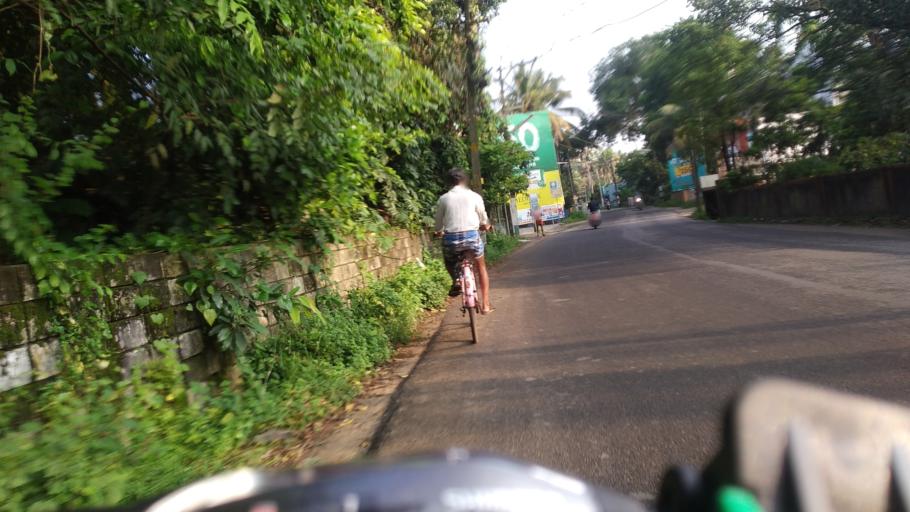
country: IN
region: Kerala
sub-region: Ernakulam
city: Elur
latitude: 10.0530
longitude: 76.2155
